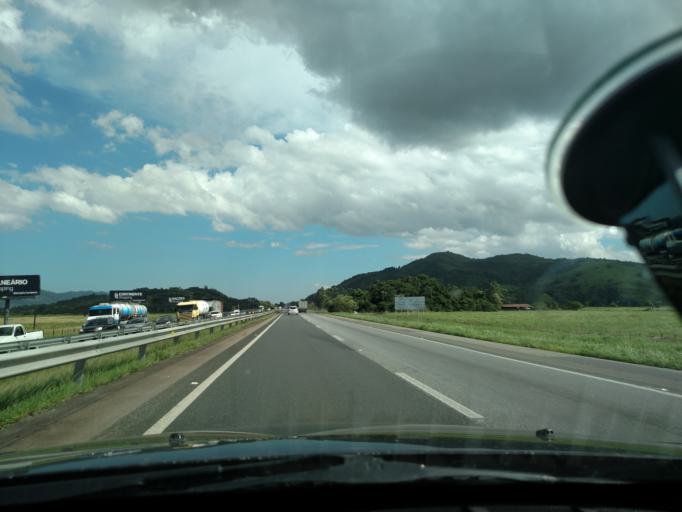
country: BR
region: Santa Catarina
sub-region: Tijucas
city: Tijucas
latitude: -27.2690
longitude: -48.6318
